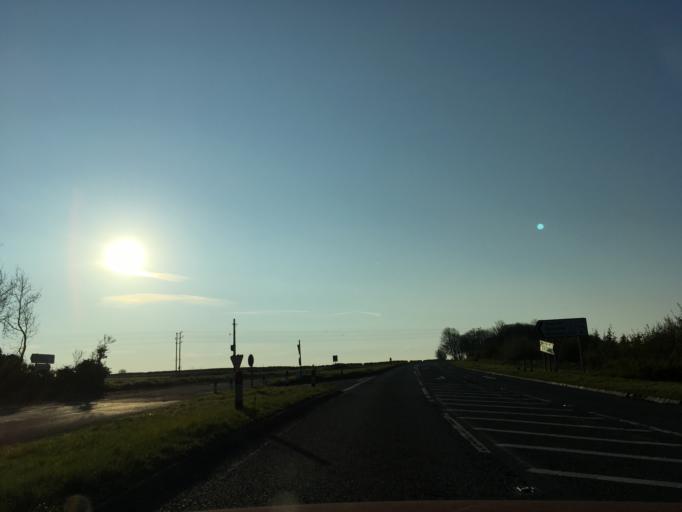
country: GB
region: England
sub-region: Gloucestershire
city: Shipton Village
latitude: 51.8582
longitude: -1.9022
